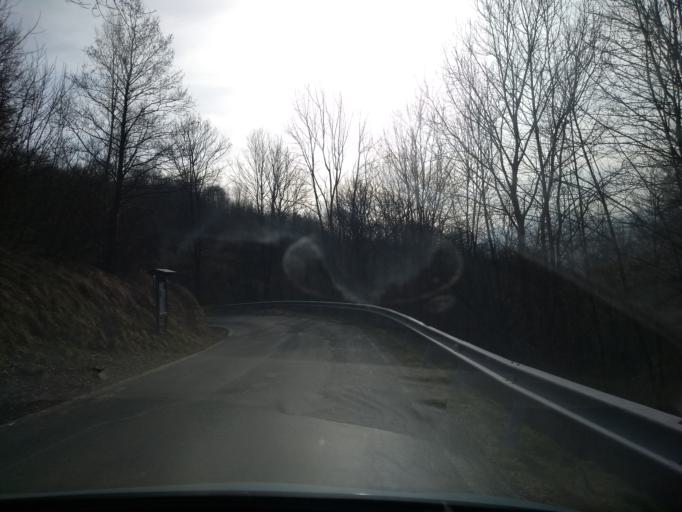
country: IT
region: Piedmont
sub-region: Provincia di Torino
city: Coassolo
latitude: 45.3122
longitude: 7.4805
